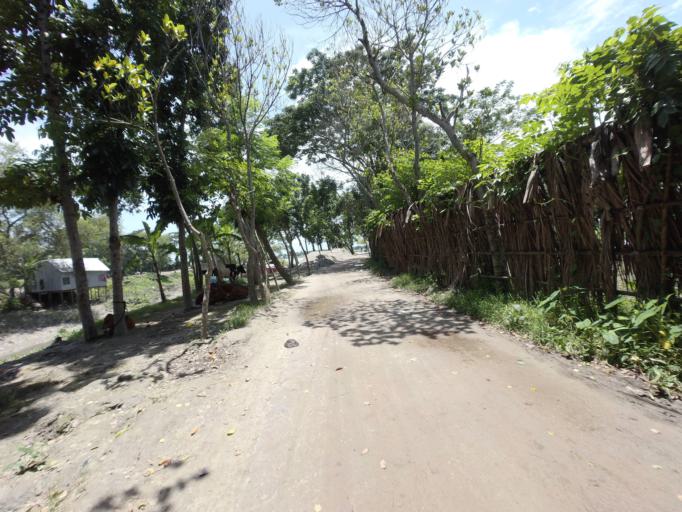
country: BD
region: Khulna
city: Kalia
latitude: 23.0442
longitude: 89.6276
